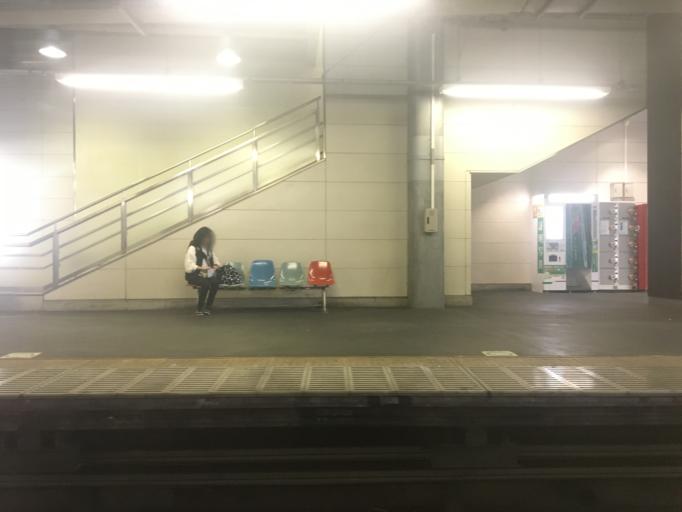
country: JP
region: Saitama
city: Sayama
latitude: 35.8575
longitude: 139.4133
